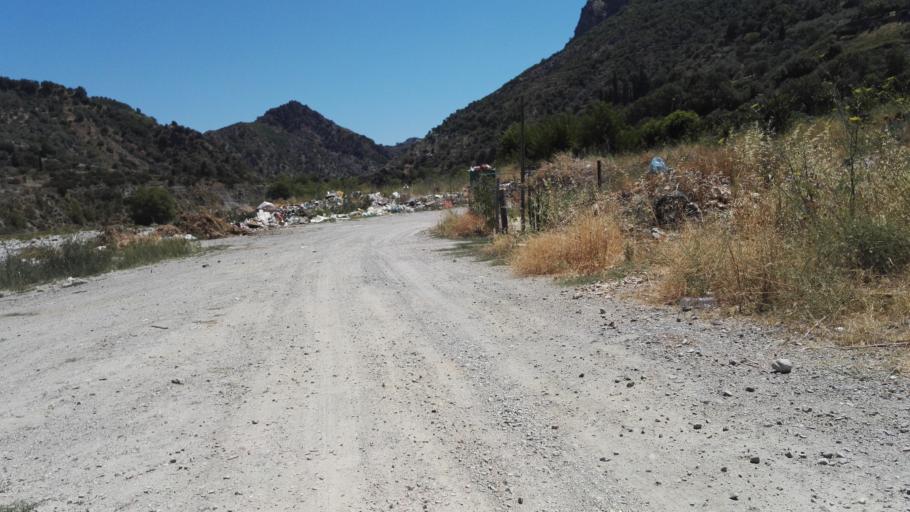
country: IT
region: Calabria
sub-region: Provincia di Reggio Calabria
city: Bivongi
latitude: 38.4864
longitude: 16.4526
